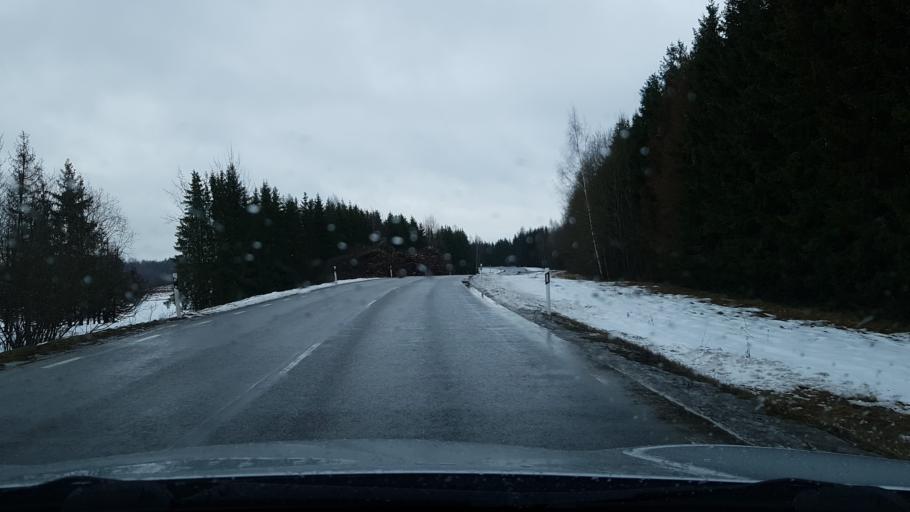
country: LV
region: Apes Novads
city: Ape
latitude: 57.5974
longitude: 26.6193
